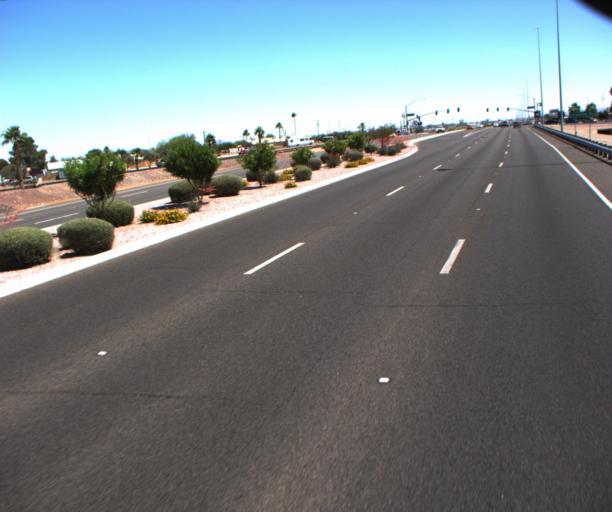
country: US
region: Arizona
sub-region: Maricopa County
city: Surprise
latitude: 33.6249
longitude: -112.3327
